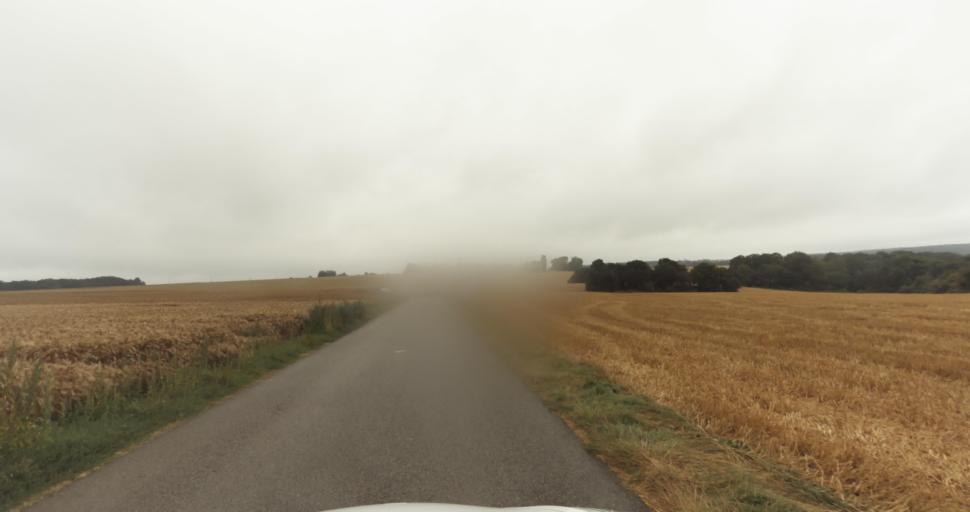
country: FR
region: Haute-Normandie
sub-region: Departement de l'Eure
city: Gravigny
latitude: 49.0770
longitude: 1.2178
